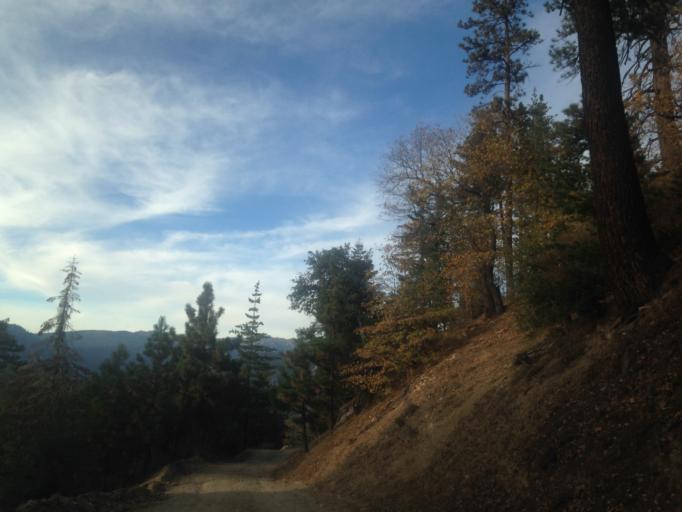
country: US
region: California
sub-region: San Bernardino County
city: Yucaipa
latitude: 34.1472
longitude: -116.9914
